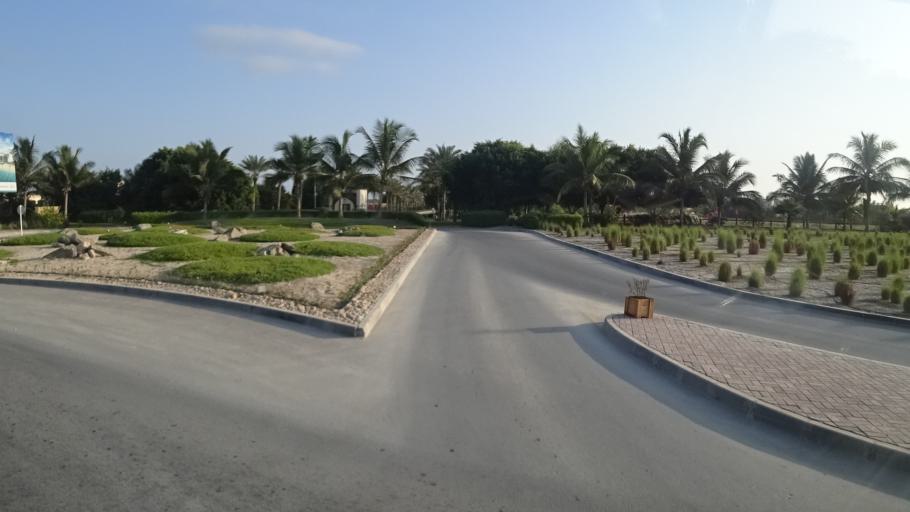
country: OM
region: Zufar
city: Salalah
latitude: 17.0390
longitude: 54.3031
